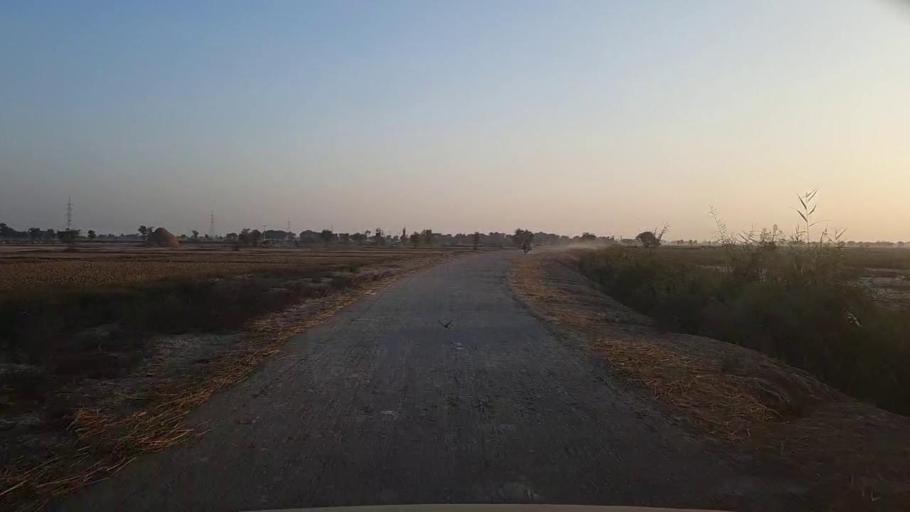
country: PK
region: Sindh
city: Khairpur Nathan Shah
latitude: 27.1768
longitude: 67.7340
